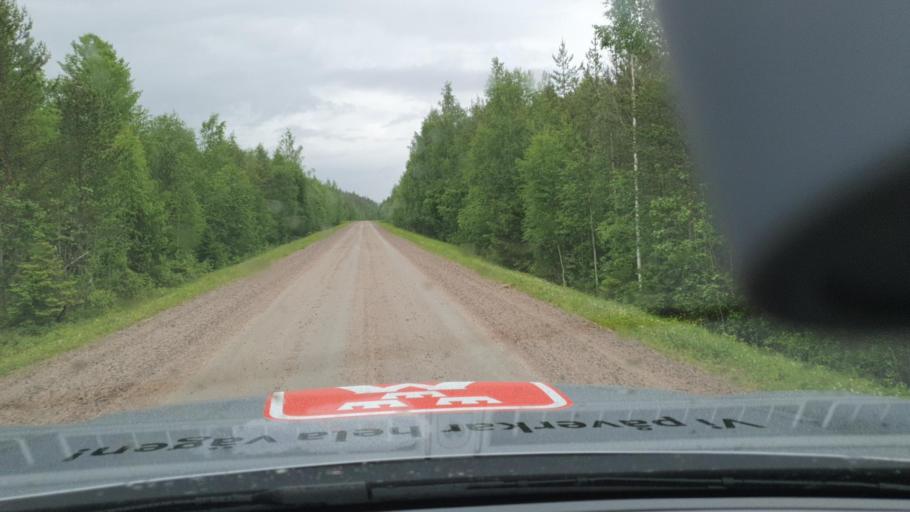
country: SE
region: Norrbotten
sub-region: Overkalix Kommun
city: OEverkalix
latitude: 66.5851
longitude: 22.7457
